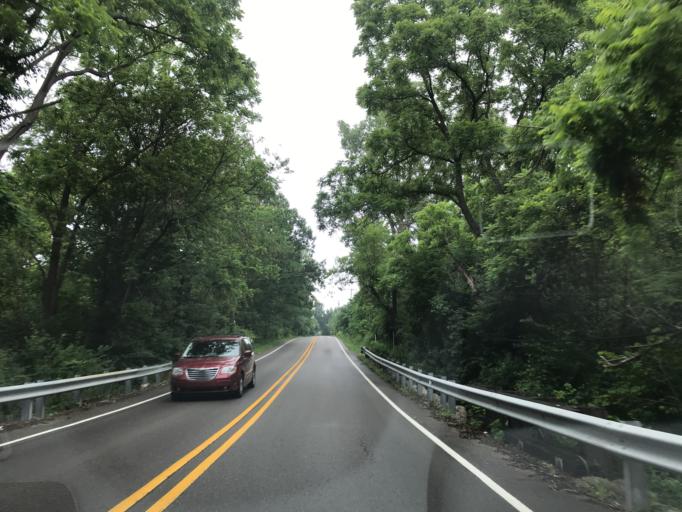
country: US
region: Michigan
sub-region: Washtenaw County
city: Ypsilanti
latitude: 42.2687
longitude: -83.6374
